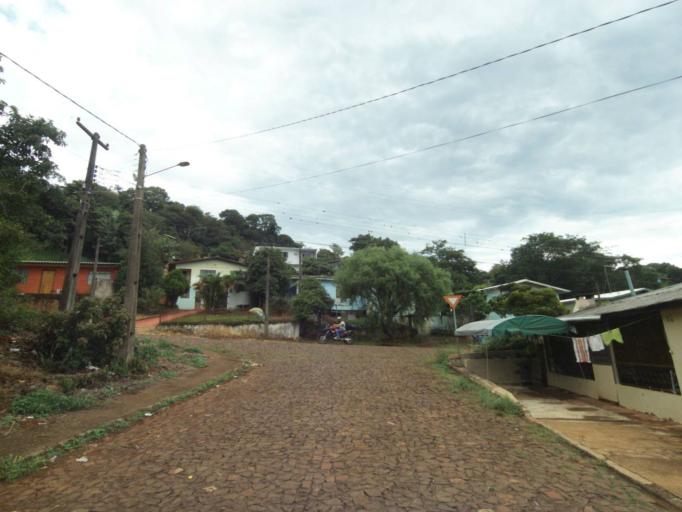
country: BR
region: Parana
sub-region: Guaraniacu
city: Guaraniacu
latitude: -25.0953
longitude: -52.8678
